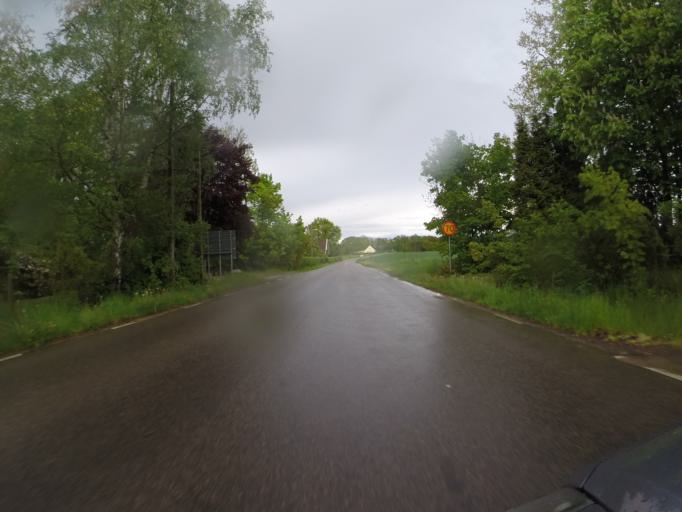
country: SE
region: Skane
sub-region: Bjuvs Kommun
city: Bjuv
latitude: 56.0731
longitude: 12.9547
